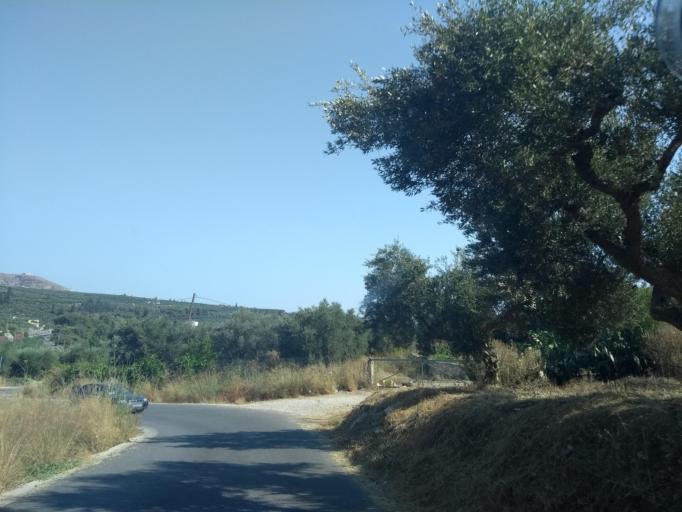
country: GR
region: Crete
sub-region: Nomos Chanias
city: Kalivai
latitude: 35.4421
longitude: 24.1718
